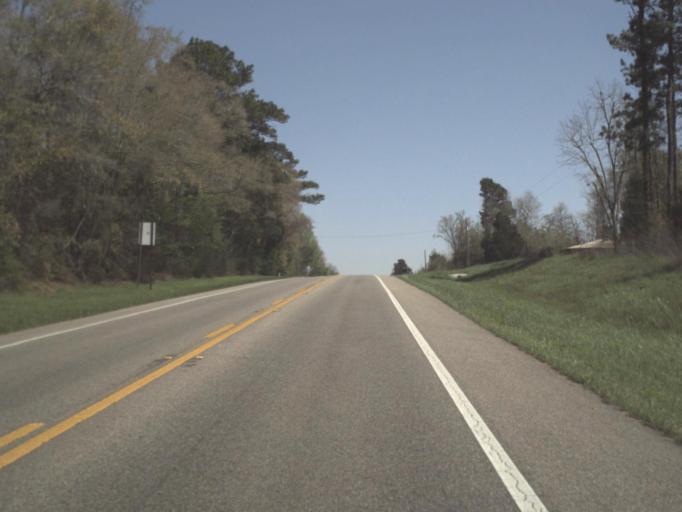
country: US
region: Florida
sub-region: Calhoun County
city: Blountstown
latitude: 30.4260
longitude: -85.1563
